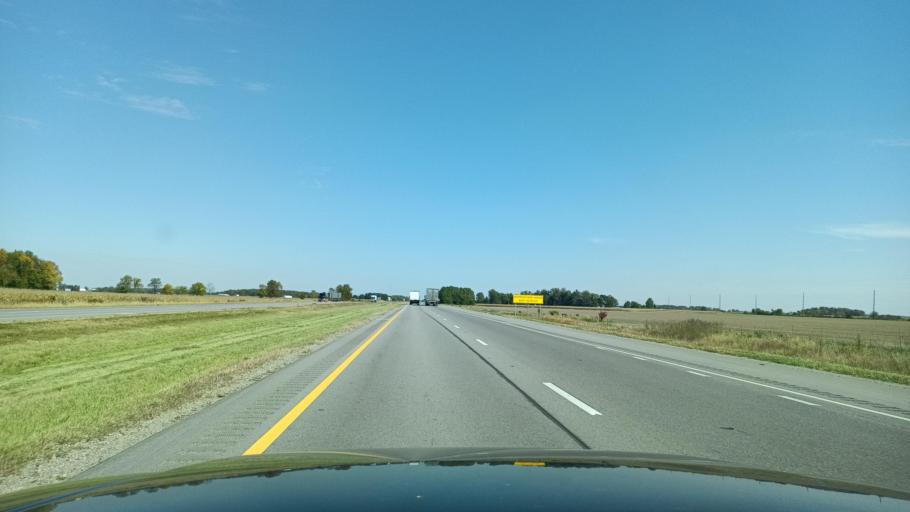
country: US
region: Ohio
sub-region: Defiance County
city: Defiance
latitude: 41.3156
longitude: -84.3162
